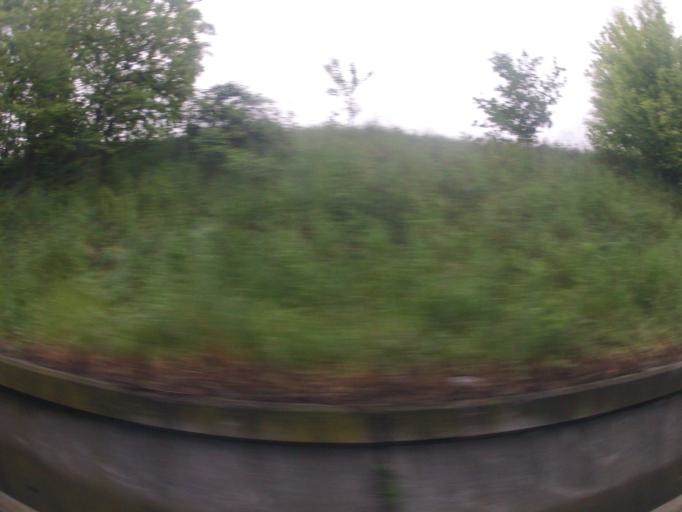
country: IT
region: Piedmont
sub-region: Provincia di Torino
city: La Loggia
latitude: 44.9554
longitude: 7.6801
